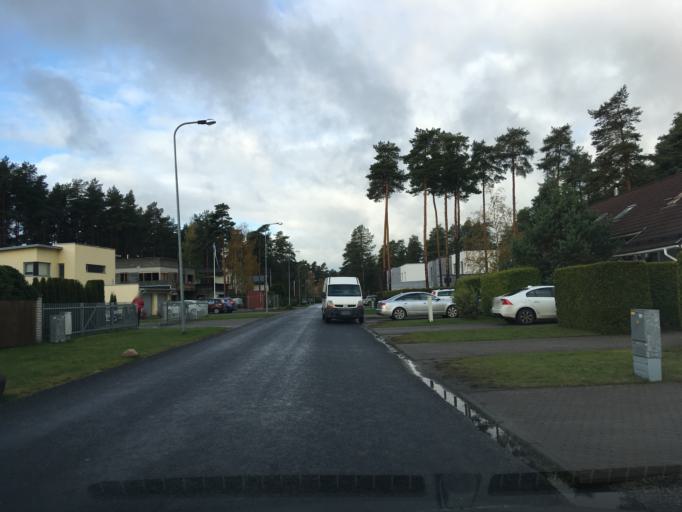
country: EE
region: Harju
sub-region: Saue vald
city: Laagri
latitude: 59.3596
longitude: 24.6115
